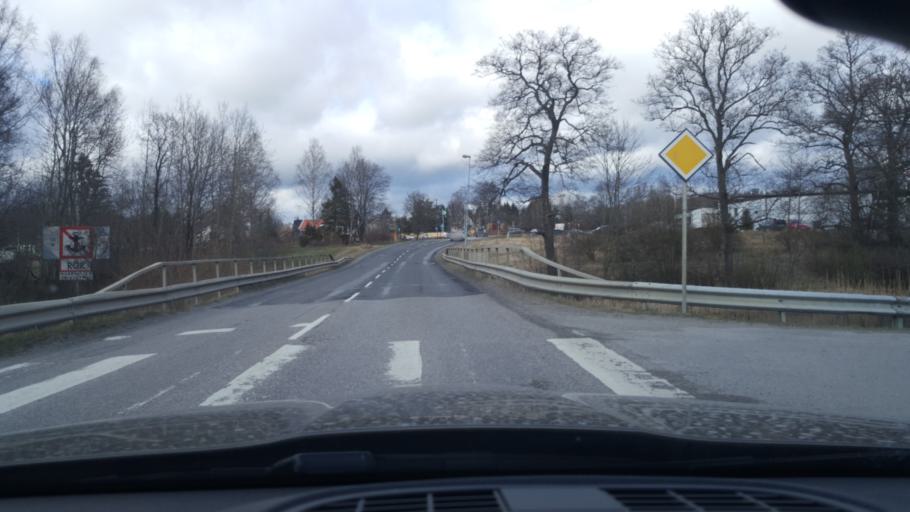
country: SE
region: Stockholm
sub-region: Osterakers Kommun
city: Akersberga
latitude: 59.4933
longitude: 18.2774
